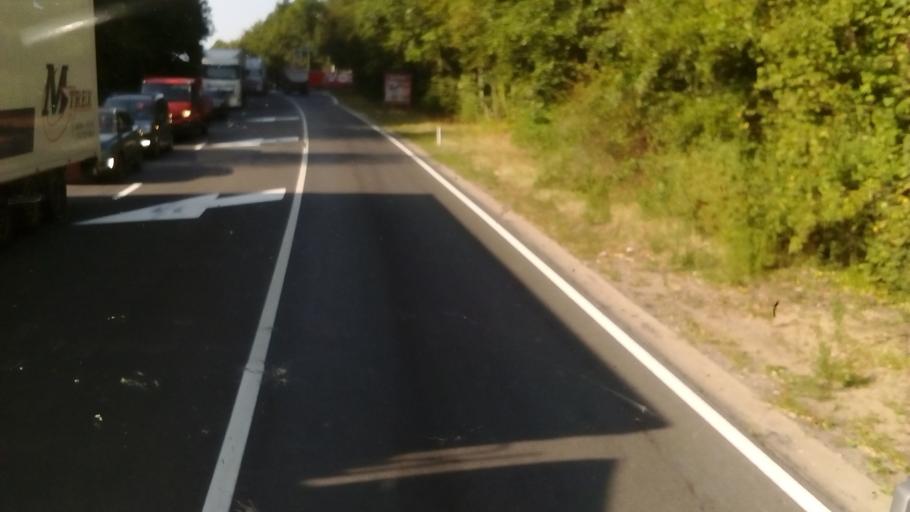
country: BE
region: Wallonia
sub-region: Province du Luxembourg
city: Aubange
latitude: 49.5539
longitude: 5.8092
